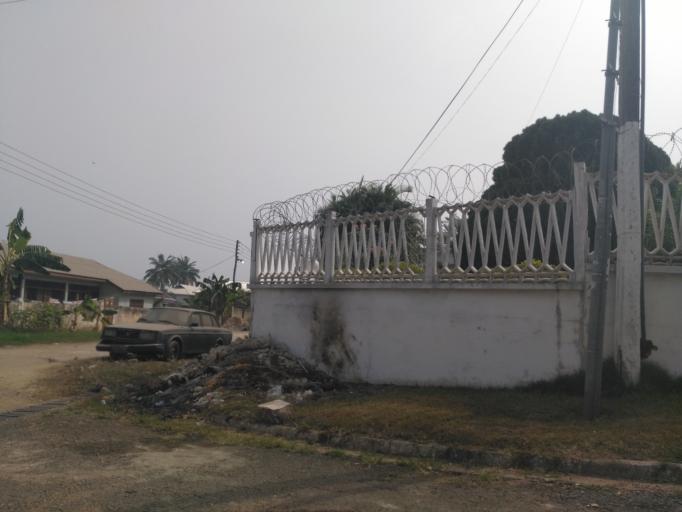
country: GH
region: Ashanti
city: Kumasi
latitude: 6.6778
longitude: -1.6044
